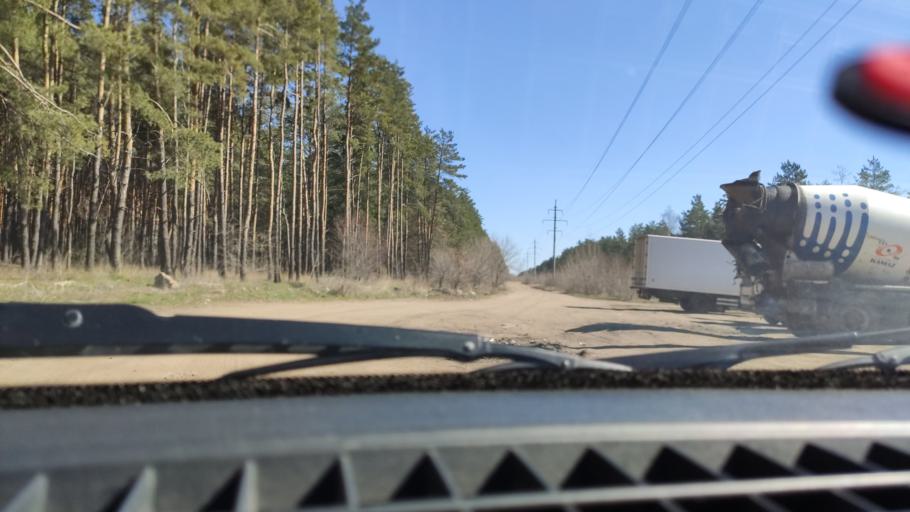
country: RU
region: Voronezj
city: Pridonskoy
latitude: 51.6880
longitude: 39.0823
